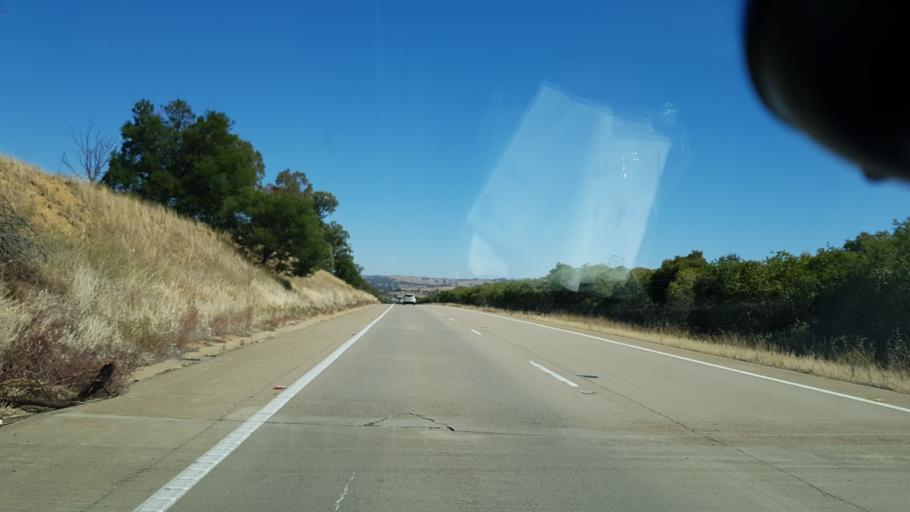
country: AU
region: New South Wales
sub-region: Gundagai
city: Gundagai
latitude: -34.8163
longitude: 148.3981
